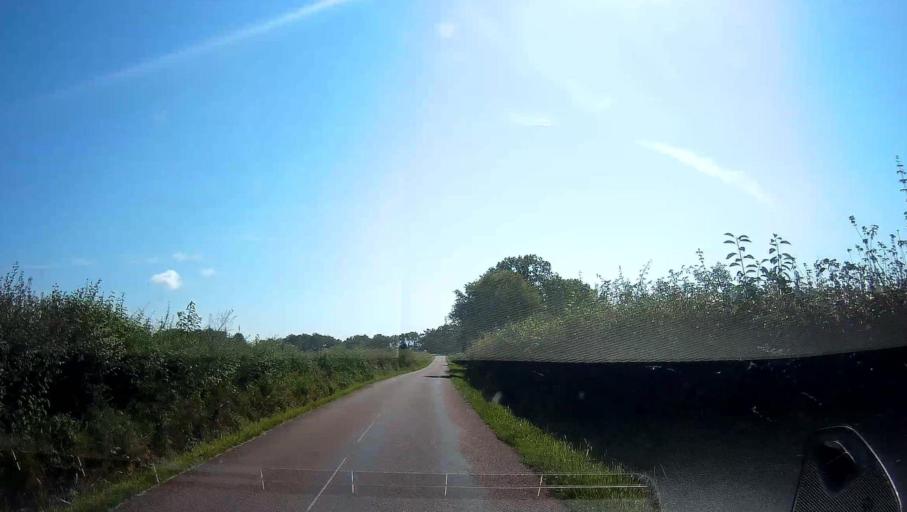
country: FR
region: Bourgogne
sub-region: Departement de Saone-et-Loire
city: Couches
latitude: 46.8843
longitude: 4.5456
